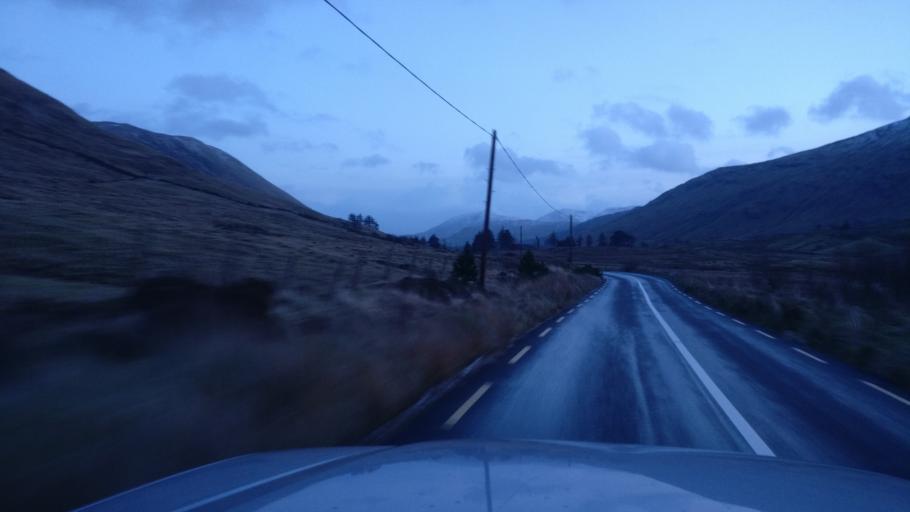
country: IE
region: Connaught
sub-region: Maigh Eo
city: Westport
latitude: 53.5808
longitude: -9.6697
